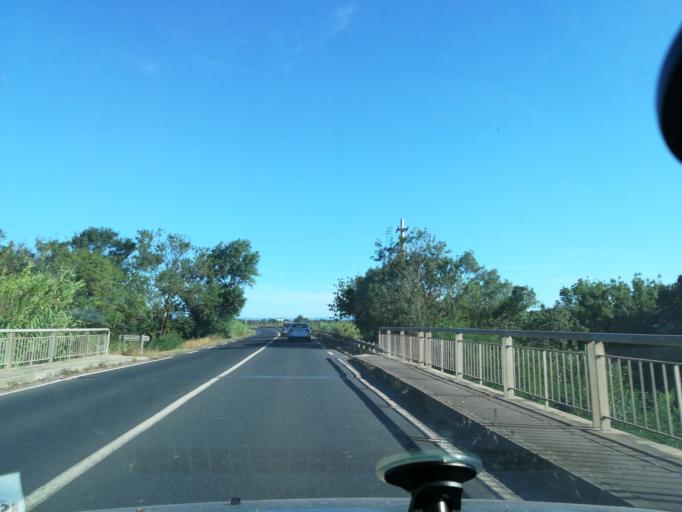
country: FR
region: Languedoc-Roussillon
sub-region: Departement de l'Herault
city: Portiragnes
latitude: 43.2911
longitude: 3.3620
